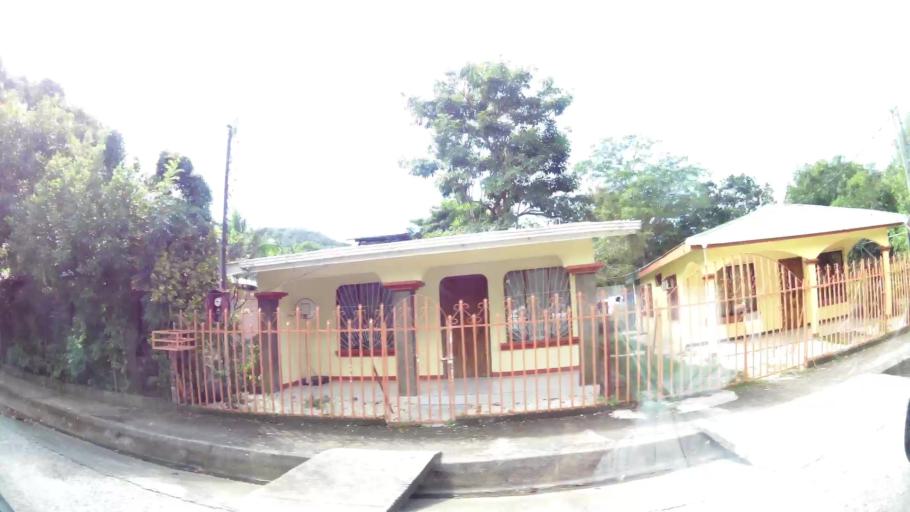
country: CR
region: Guanacaste
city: Juntas
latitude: 10.2807
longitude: -84.9469
